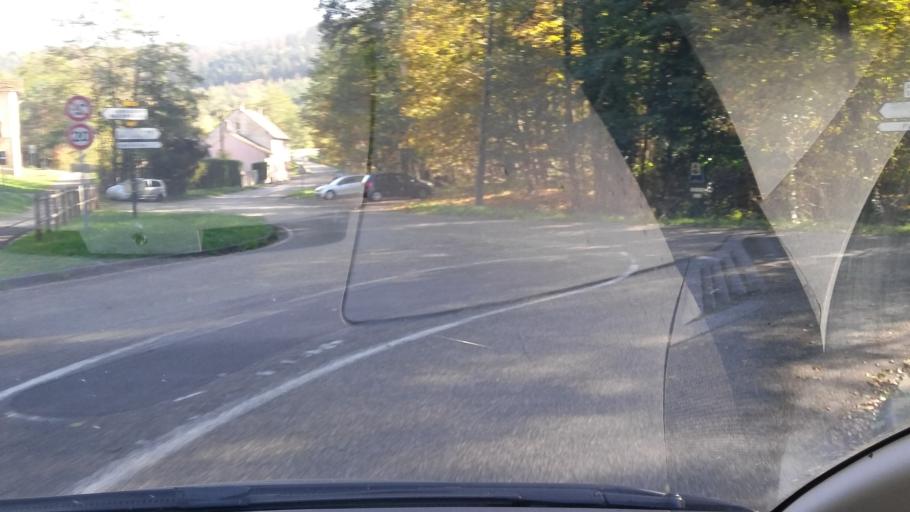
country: FR
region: Lorraine
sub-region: Departement de la Moselle
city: Phalsbourg
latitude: 48.7198
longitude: 7.2205
